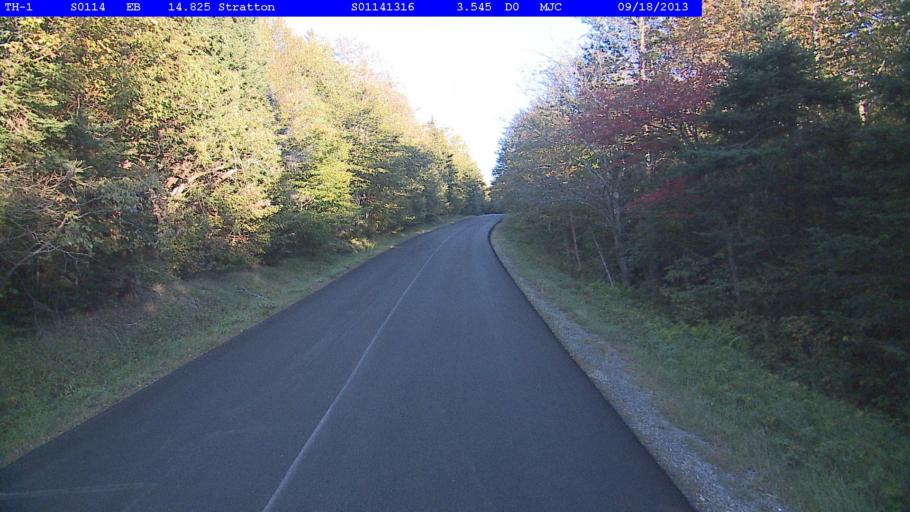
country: US
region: Vermont
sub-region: Bennington County
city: Manchester Center
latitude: 43.0565
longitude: -72.9372
